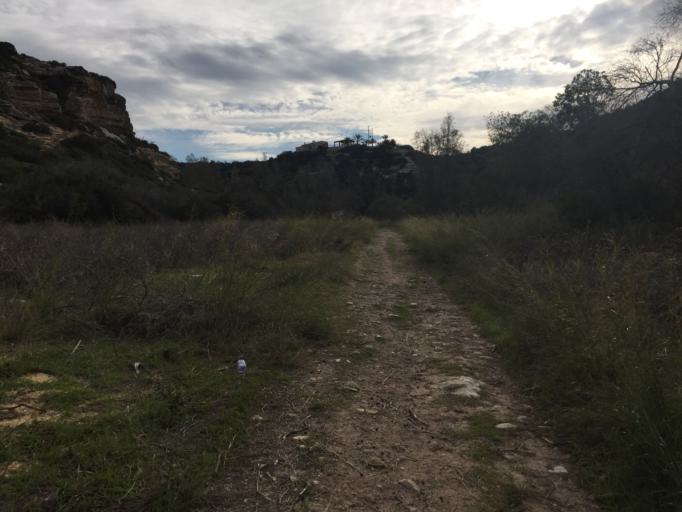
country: CY
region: Pafos
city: Pegeia
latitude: 34.9182
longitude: 32.3311
